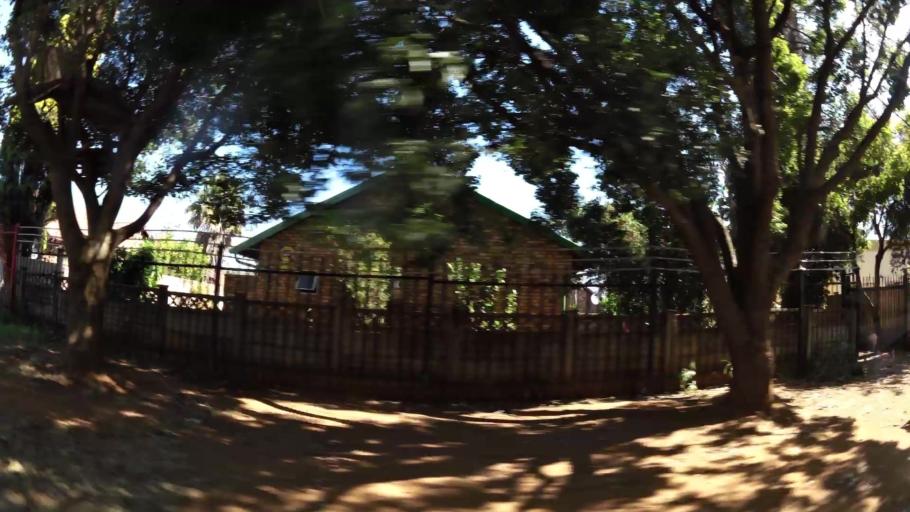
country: ZA
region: Gauteng
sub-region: City of Tshwane Metropolitan Municipality
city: Pretoria
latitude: -25.6515
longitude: 28.2535
